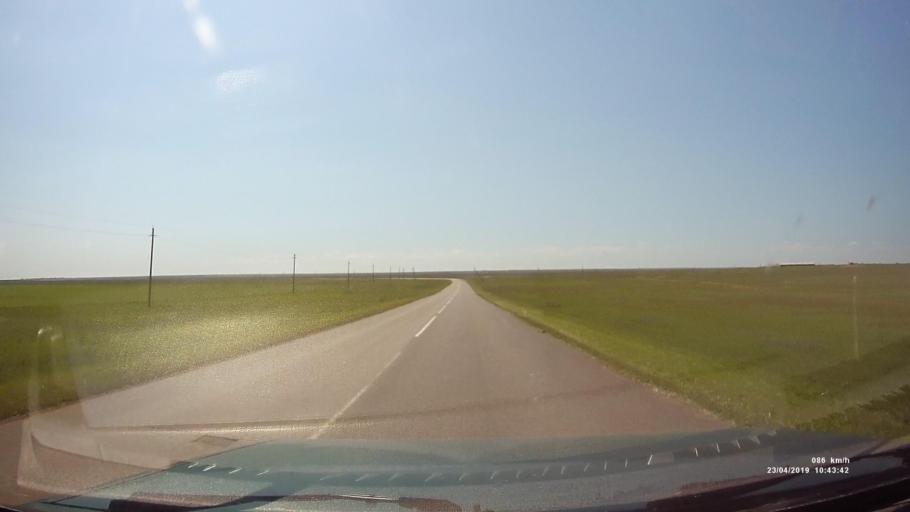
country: RU
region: Kalmykiya
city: Yashalta
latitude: 46.4671
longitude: 42.6501
